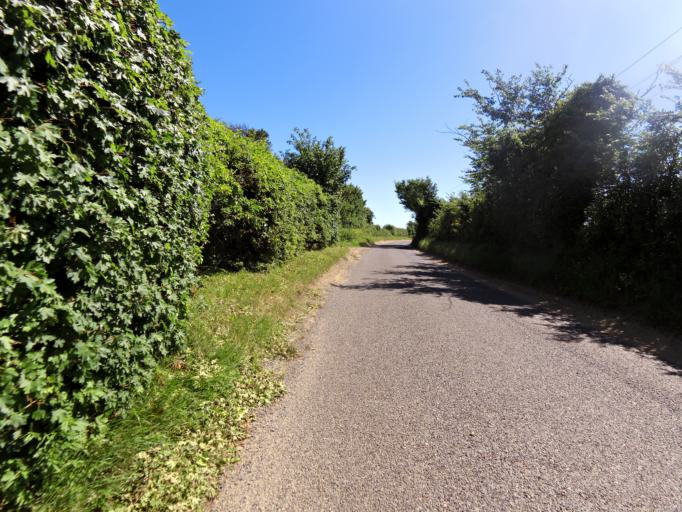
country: GB
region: England
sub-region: Suffolk
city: Felixstowe
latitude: 52.0332
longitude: 1.4171
